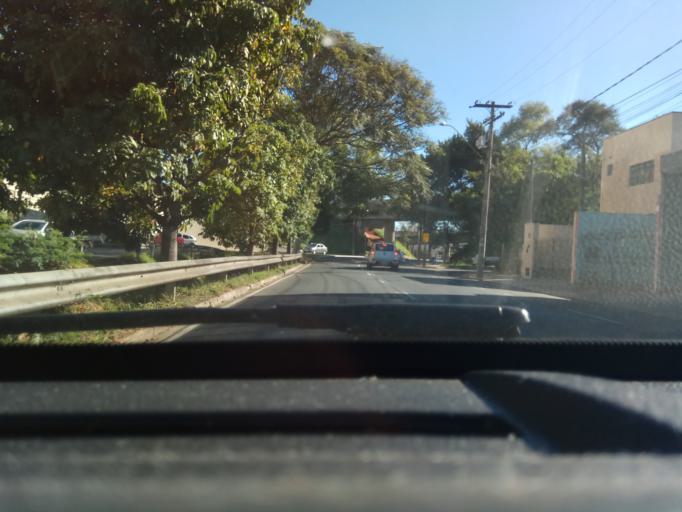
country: BR
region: Sao Paulo
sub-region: Piracicaba
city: Piracicaba
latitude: -22.7404
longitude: -47.6468
